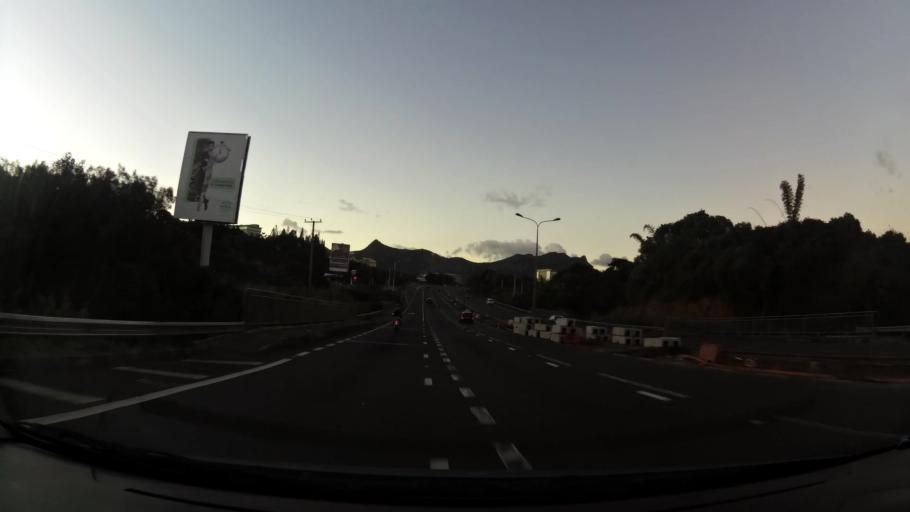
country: MU
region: Plaines Wilhems
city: Ebene
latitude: -20.2402
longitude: 57.4982
